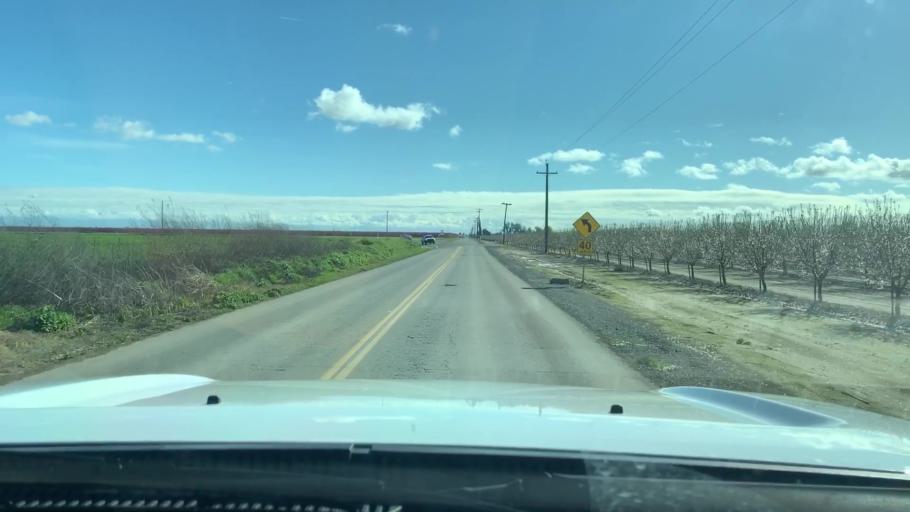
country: US
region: California
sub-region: Fresno County
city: Laton
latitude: 36.4893
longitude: -119.6861
